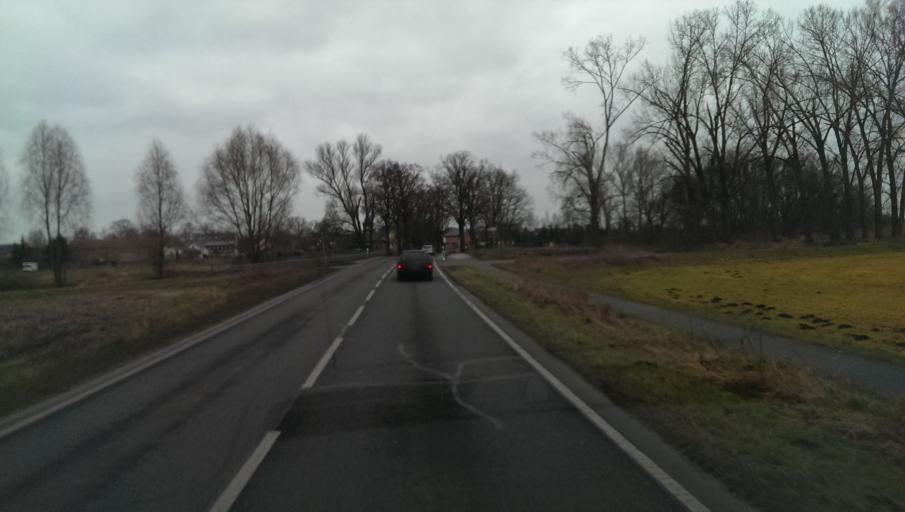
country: DE
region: Brandenburg
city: Ludwigsfelde
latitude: 52.2729
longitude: 13.3032
